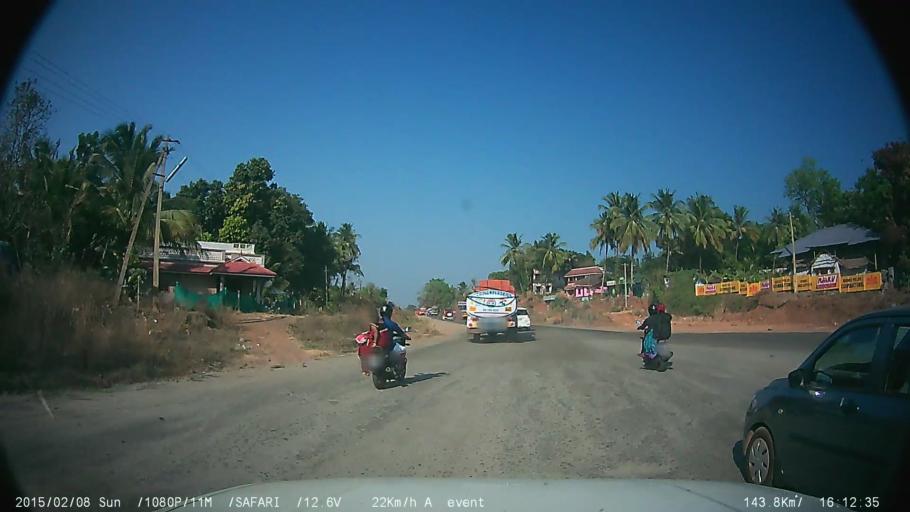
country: IN
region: Kerala
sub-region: Thrissur District
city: Chelakara
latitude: 10.6067
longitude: 76.4954
